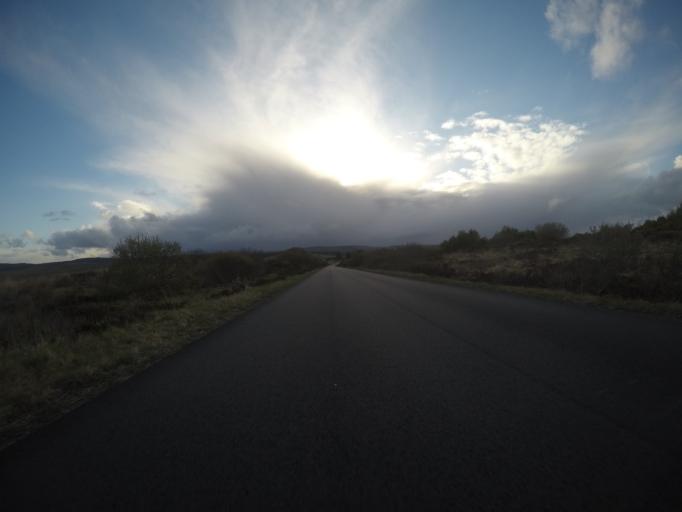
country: GB
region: Scotland
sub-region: Highland
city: Portree
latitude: 57.4506
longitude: -6.2761
